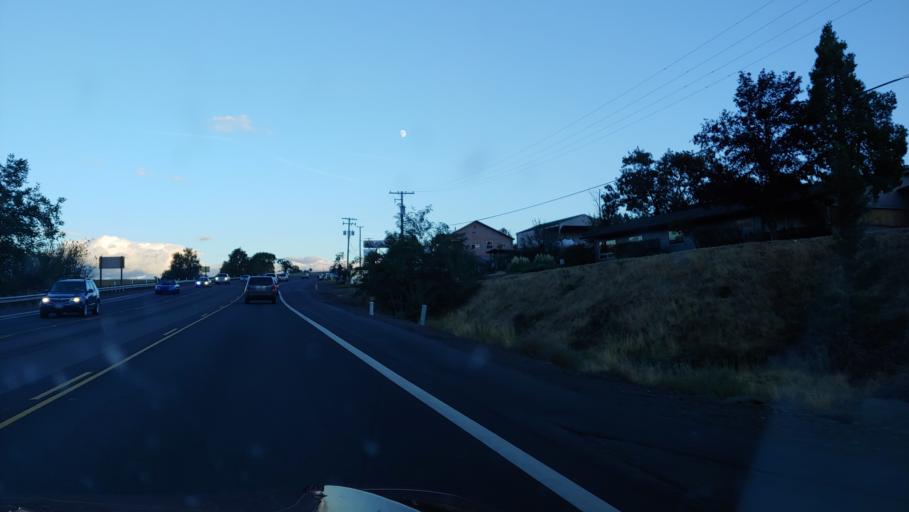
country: US
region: Oregon
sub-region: Jackson County
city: Ashland
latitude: 42.2179
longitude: -122.7354
